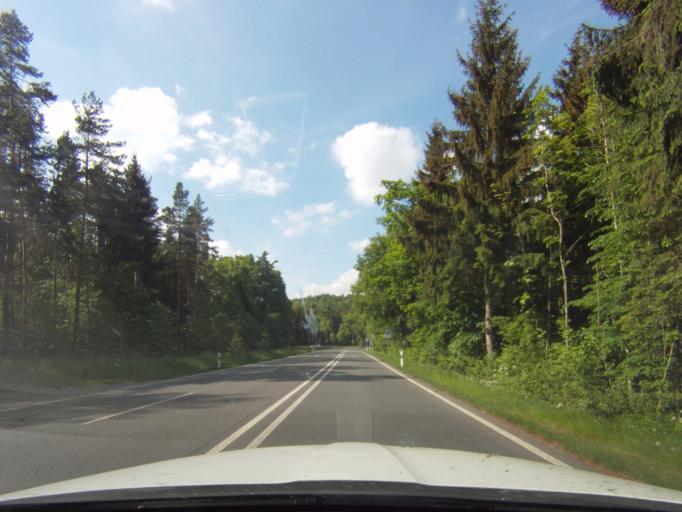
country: DE
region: Thuringia
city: Gera
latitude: 50.8657
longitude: 12.0431
